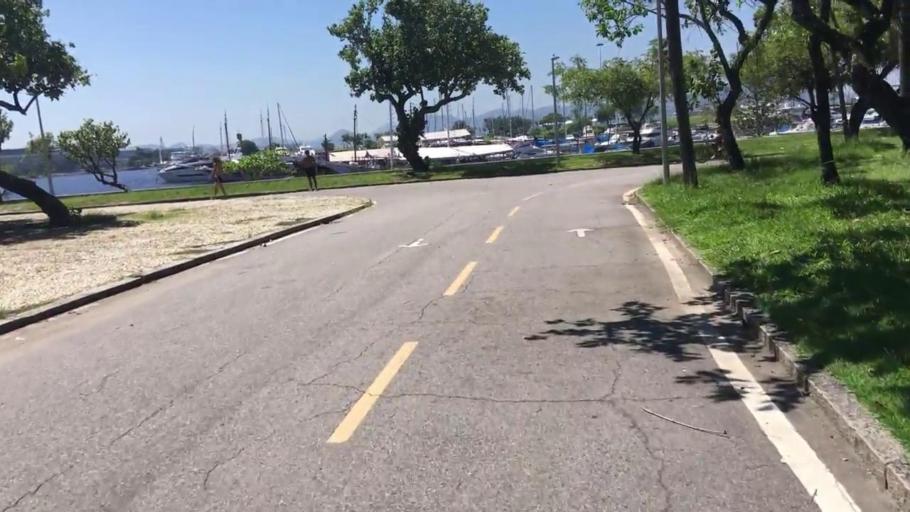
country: BR
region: Rio de Janeiro
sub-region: Rio De Janeiro
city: Rio de Janeiro
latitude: -22.9178
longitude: -43.1733
